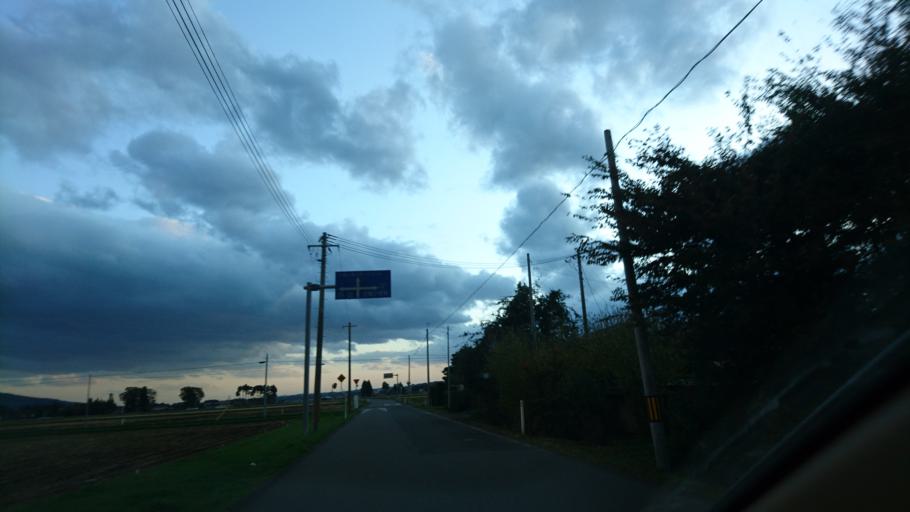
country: JP
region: Iwate
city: Mizusawa
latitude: 39.0781
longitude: 141.1422
